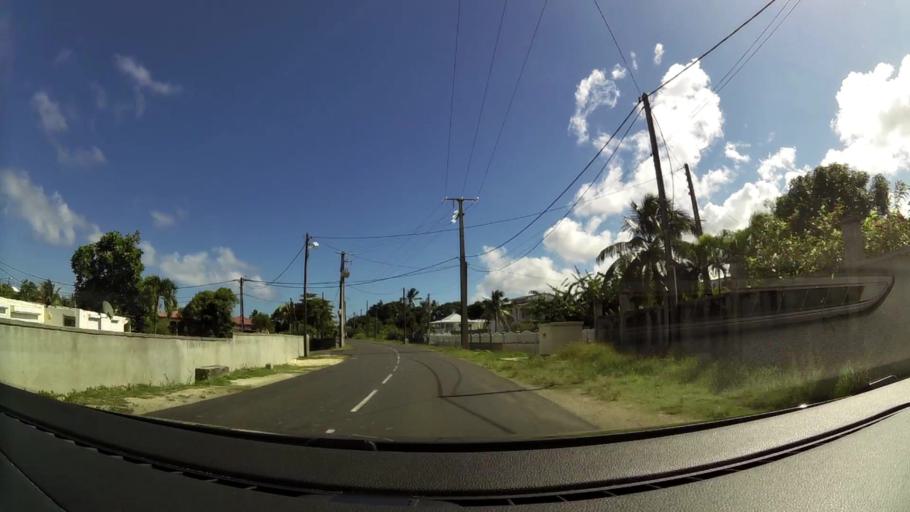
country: GP
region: Guadeloupe
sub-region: Guadeloupe
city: Petit-Canal
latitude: 16.3692
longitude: -61.4440
